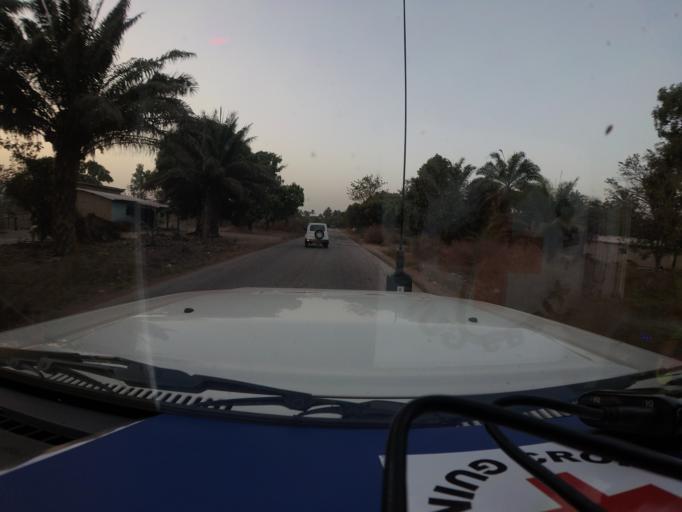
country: GN
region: Kindia
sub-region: Kindia
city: Kindia
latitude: 9.8767
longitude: -13.0533
